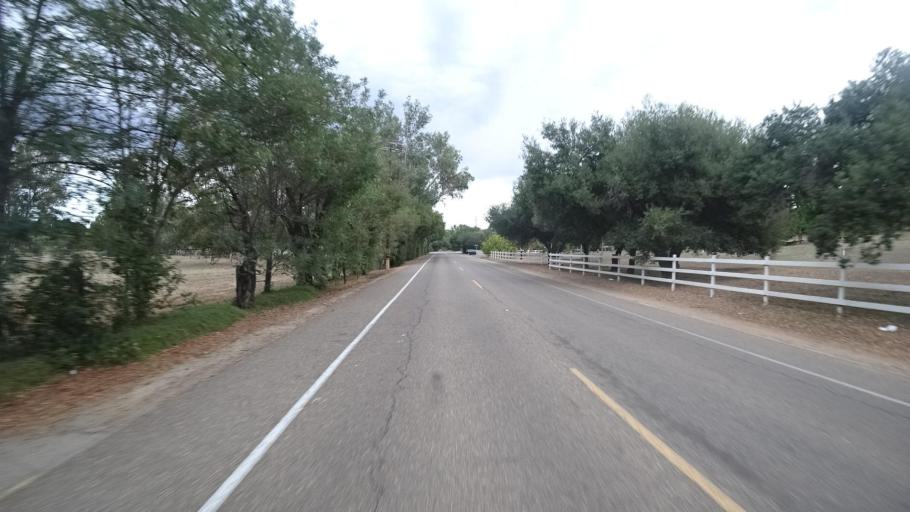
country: US
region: California
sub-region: San Diego County
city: Ramona
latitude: 33.0030
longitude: -116.9215
